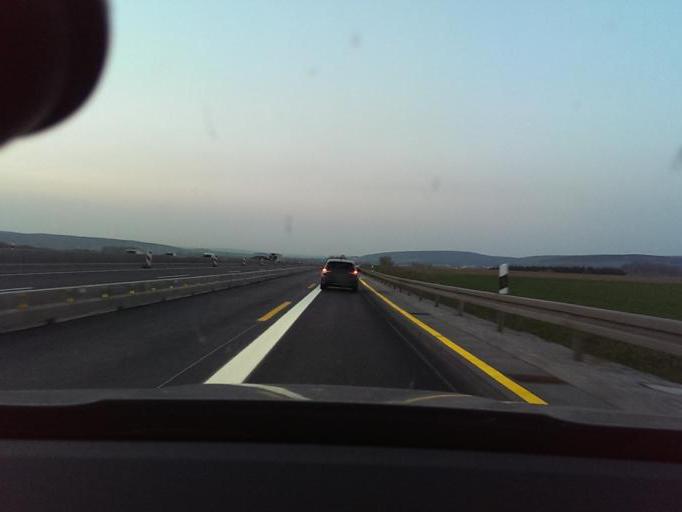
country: DE
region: Lower Saxony
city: Seesen
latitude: 51.9070
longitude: 10.1339
